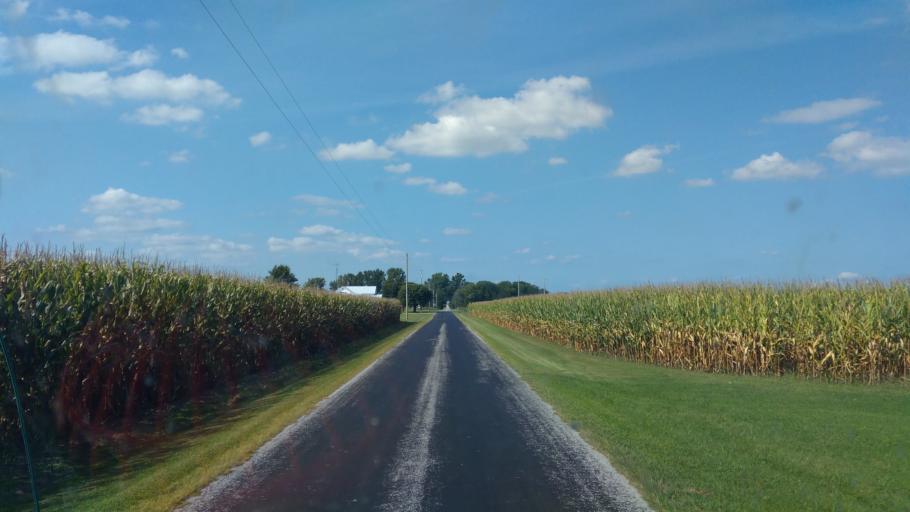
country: US
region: Ohio
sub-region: Hardin County
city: Forest
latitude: 40.7069
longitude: -83.4779
